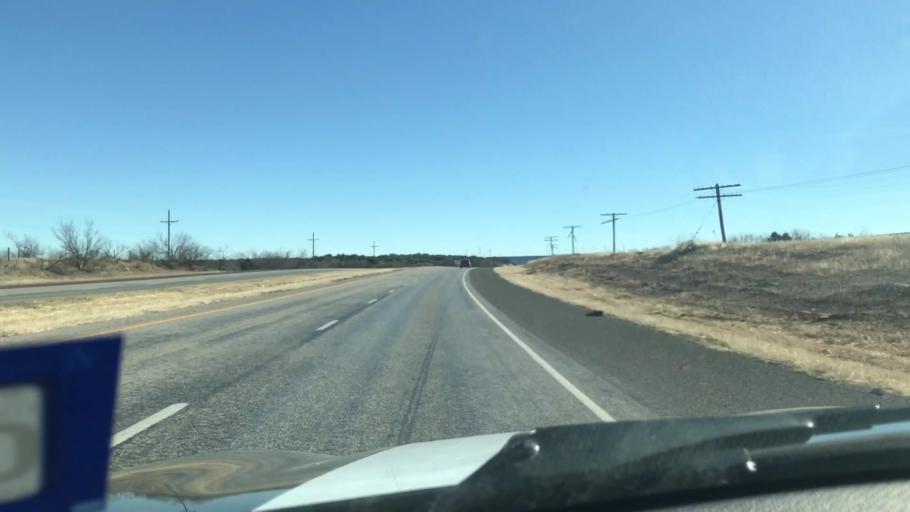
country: US
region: Texas
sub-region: Garza County
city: Post
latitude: 33.0273
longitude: -101.1856
